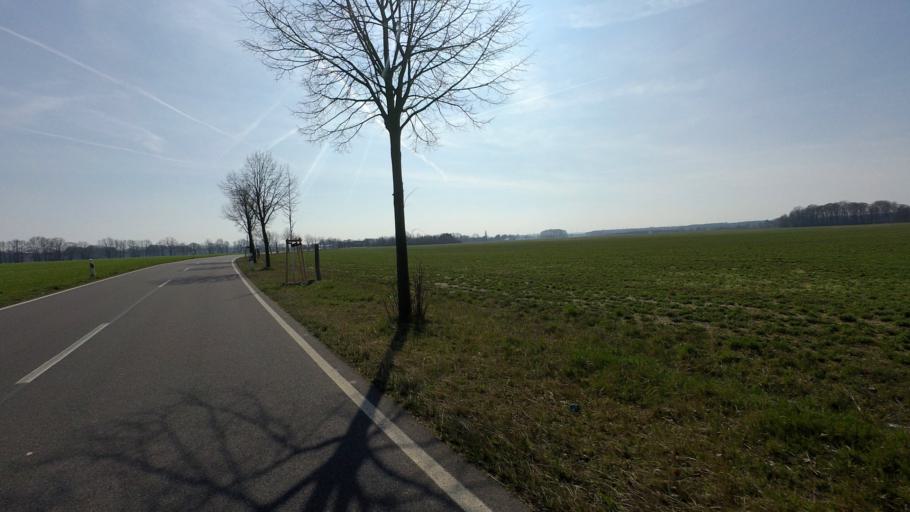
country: DE
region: Brandenburg
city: Golssen
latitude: 51.9480
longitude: 13.5983
